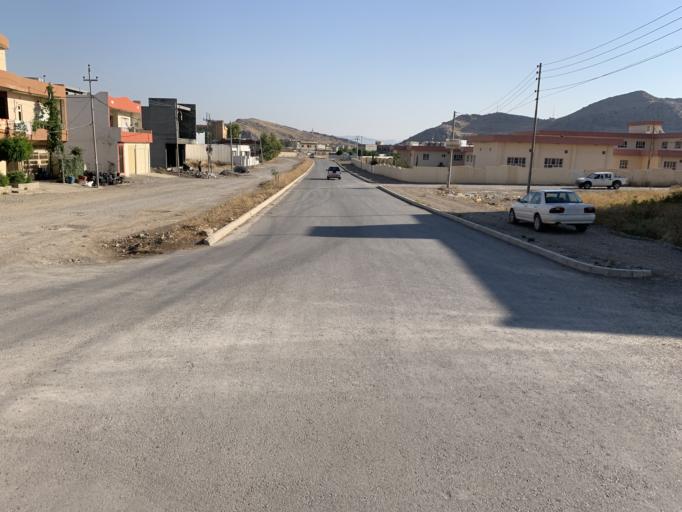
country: IQ
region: As Sulaymaniyah
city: Raniye
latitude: 36.2423
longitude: 44.8720
